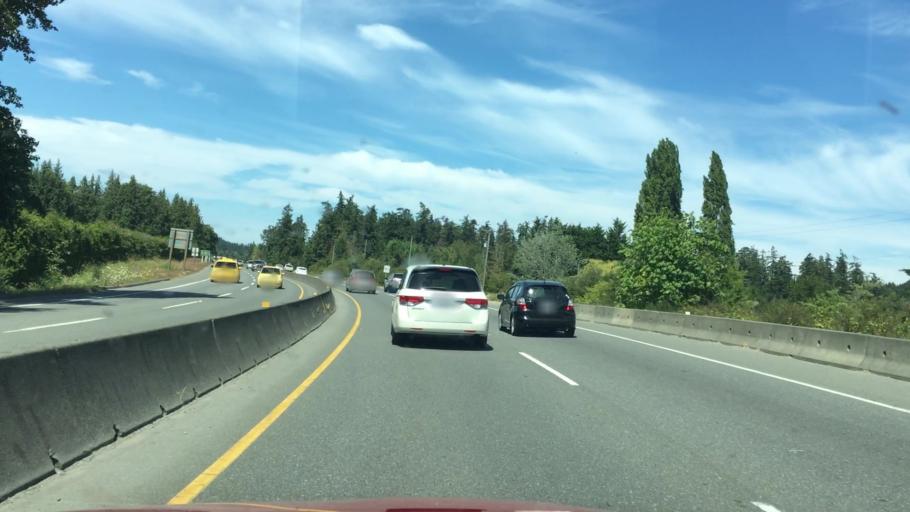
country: CA
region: British Columbia
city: North Saanich
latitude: 48.5762
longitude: -123.3985
